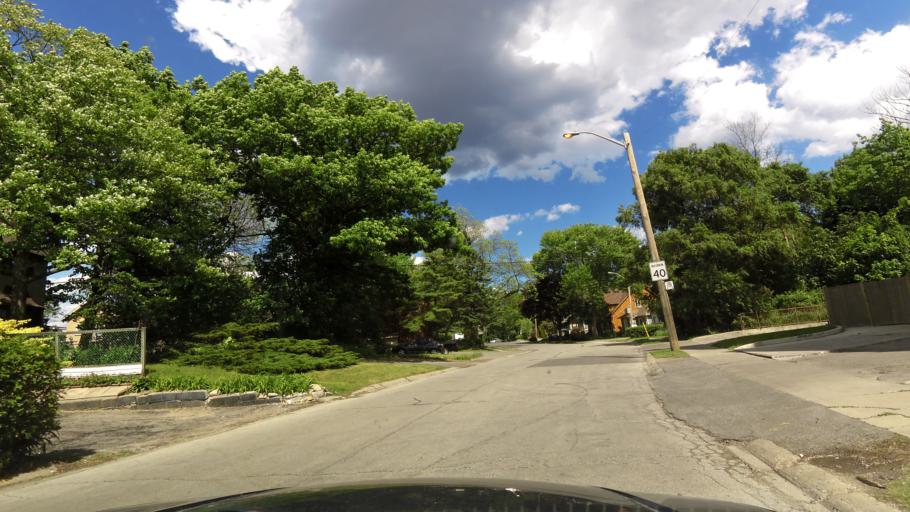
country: CA
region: Ontario
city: Etobicoke
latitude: 43.5910
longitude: -79.5303
